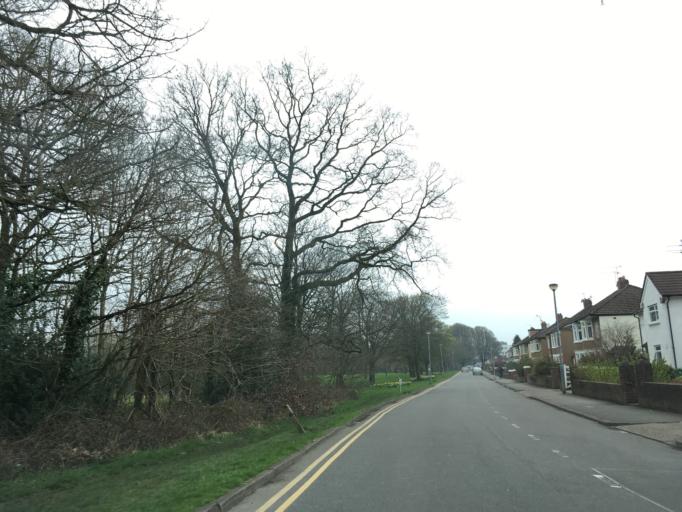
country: GB
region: Wales
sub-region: Cardiff
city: Cardiff
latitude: 51.5117
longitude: -3.1920
